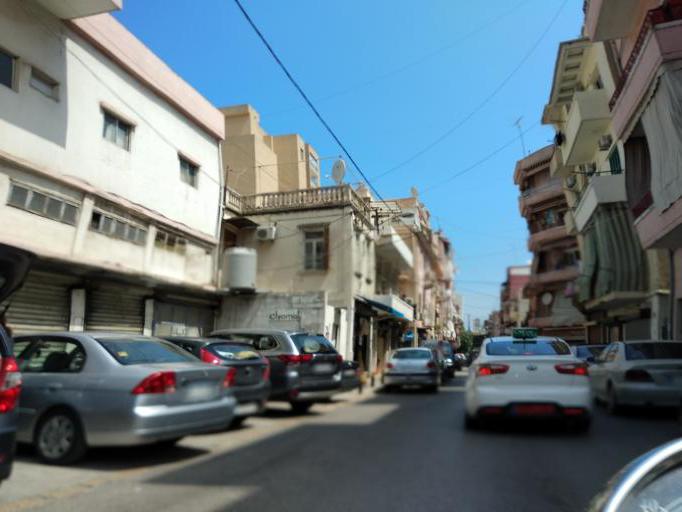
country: LB
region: Mont-Liban
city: Jdaidet el Matn
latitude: 33.8944
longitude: 35.5338
